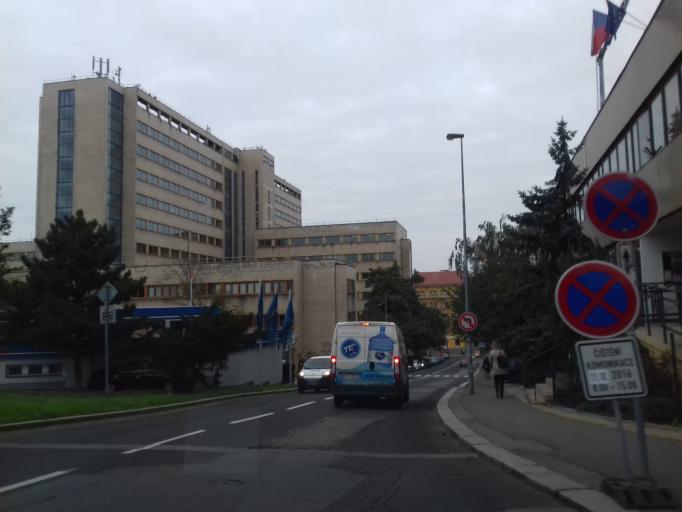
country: CZ
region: Praha
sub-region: Praha 8
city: Karlin
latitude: 50.0834
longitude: 14.4433
